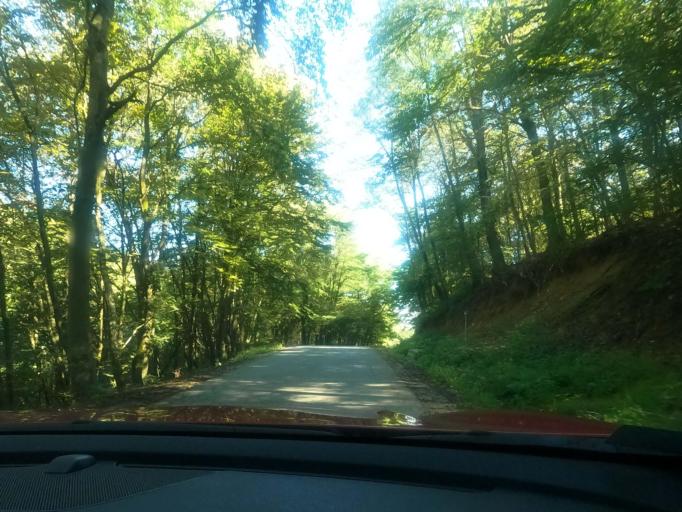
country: HR
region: Sisacko-Moslavacka
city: Petrinja
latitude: 45.4088
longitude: 16.2475
